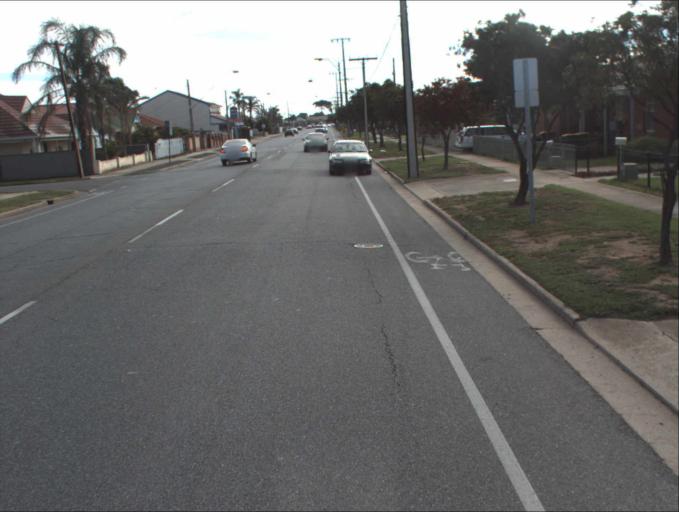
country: AU
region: South Australia
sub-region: Port Adelaide Enfield
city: Alberton
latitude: -34.8559
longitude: 138.5291
